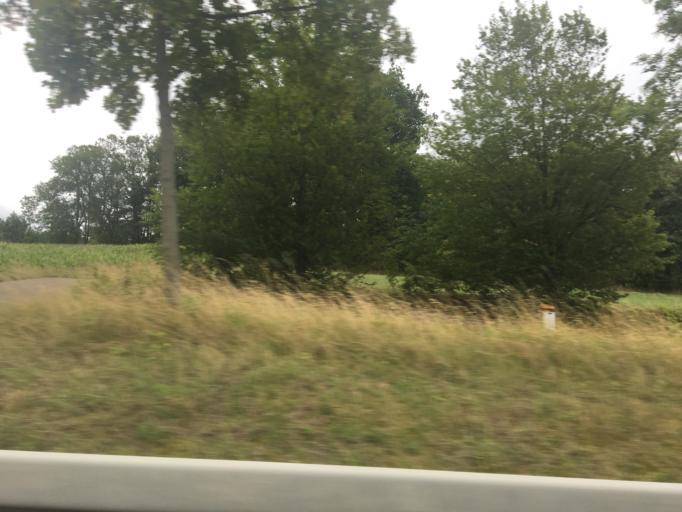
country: DE
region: Bavaria
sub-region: Upper Franconia
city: Feilitzsch
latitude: 50.3361
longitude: 11.9366
